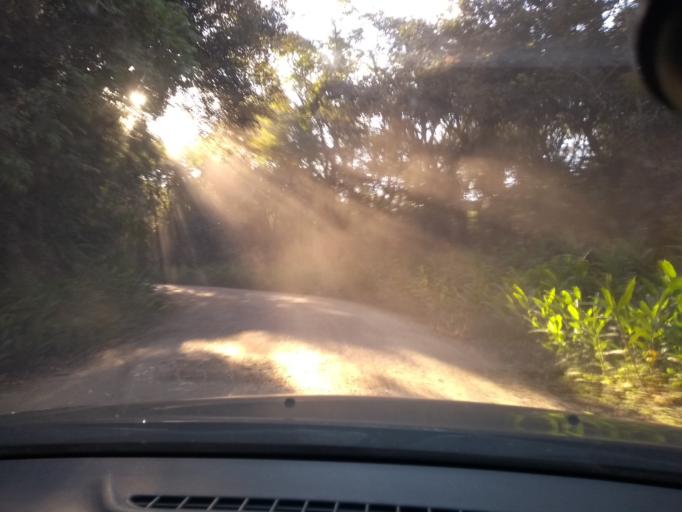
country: BR
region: Sao Paulo
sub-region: Rio Grande Da Serra
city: Rio Grande da Serra
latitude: -23.7784
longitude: -46.4903
